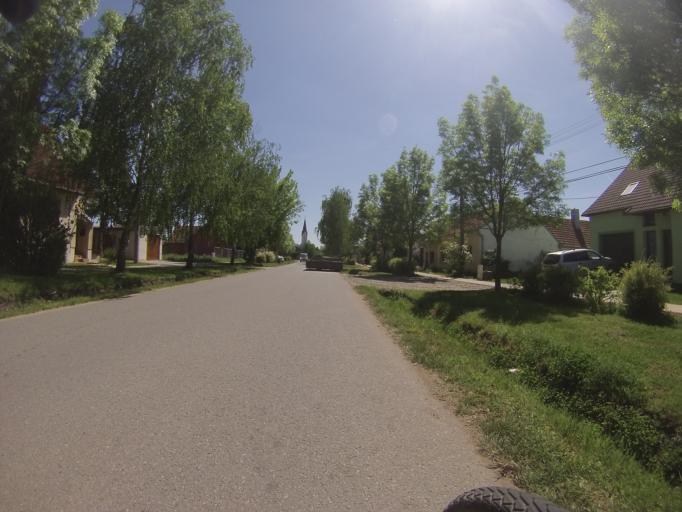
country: CZ
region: South Moravian
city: Novosedly
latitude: 48.8100
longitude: 16.4935
